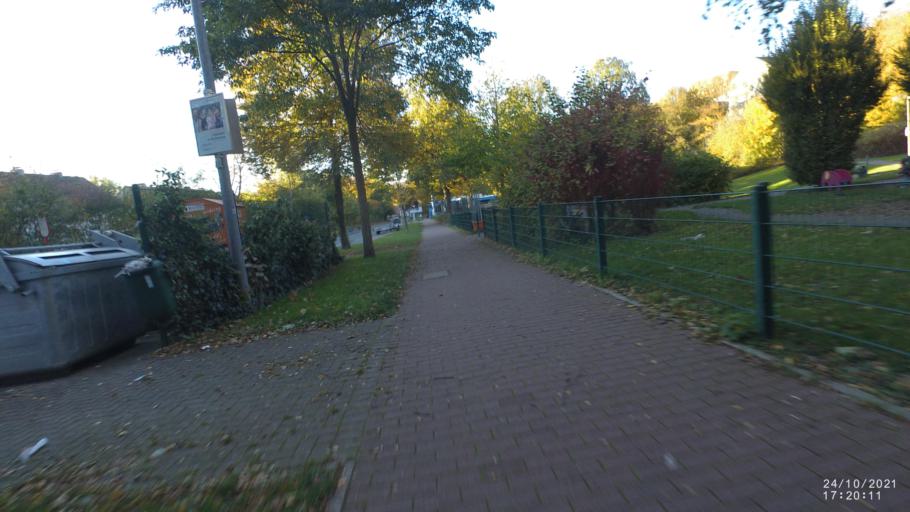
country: DE
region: North Rhine-Westphalia
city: Iserlohn
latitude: 51.3769
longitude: 7.7302
